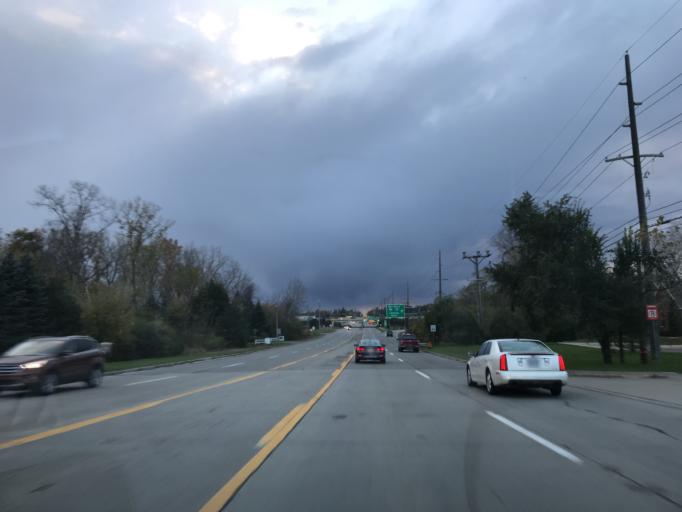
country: US
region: Michigan
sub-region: Oakland County
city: Farmington
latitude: 42.4392
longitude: -83.4261
